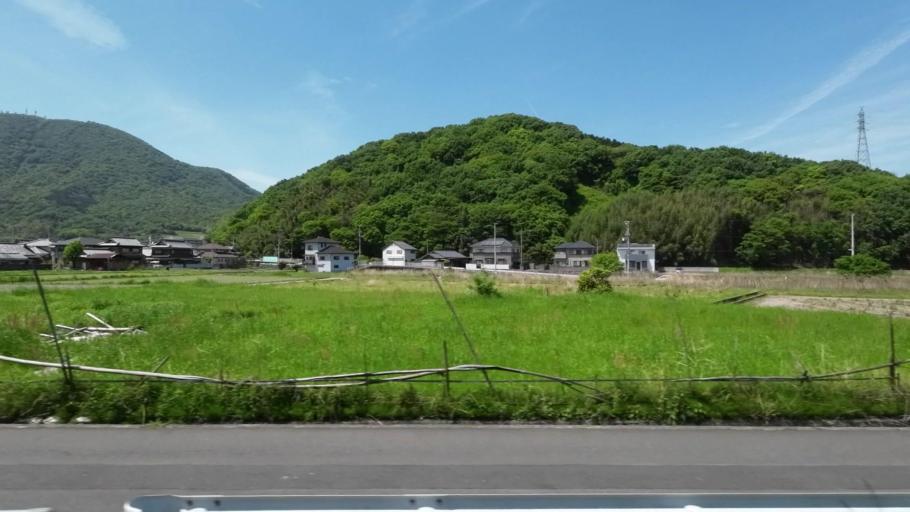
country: JP
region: Kagawa
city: Marugame
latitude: 34.2212
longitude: 133.7951
